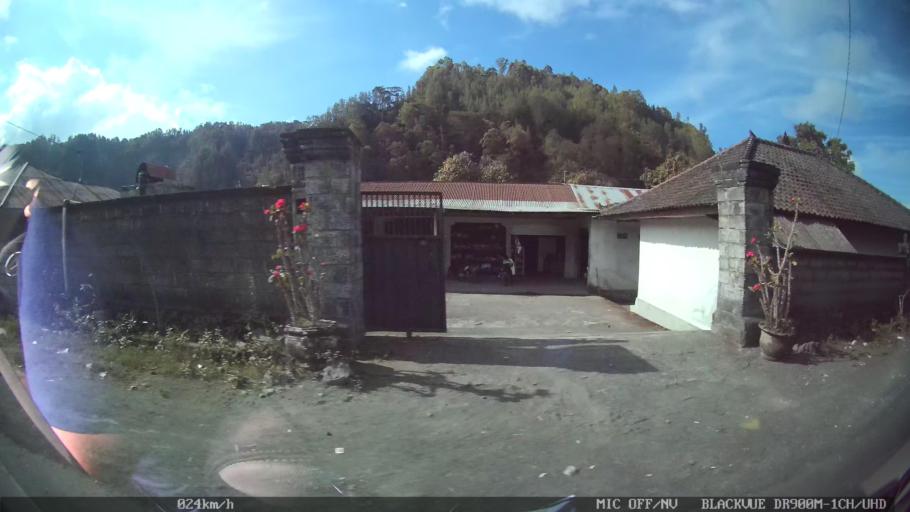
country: ID
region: Bali
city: Banjar Trunyan
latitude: -8.2148
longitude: 115.3742
